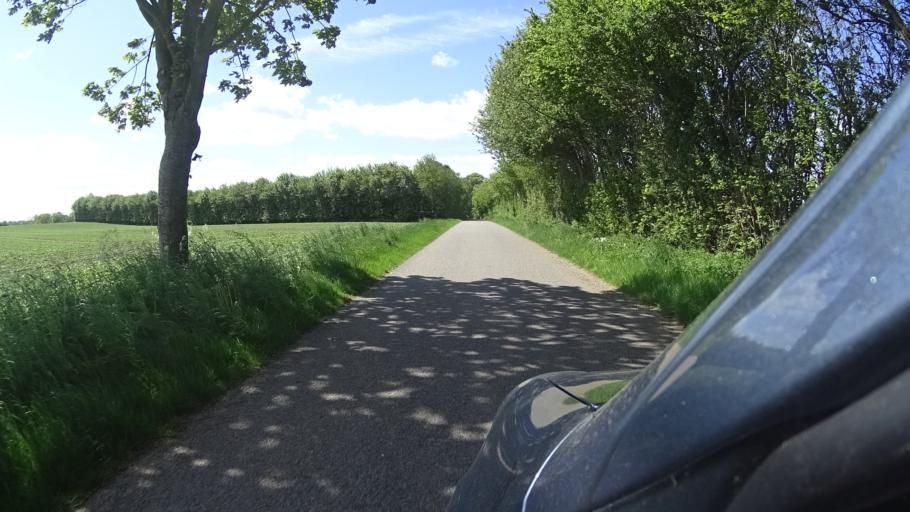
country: DK
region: South Denmark
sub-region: Vejle Kommune
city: Borkop
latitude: 55.6139
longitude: 9.6542
